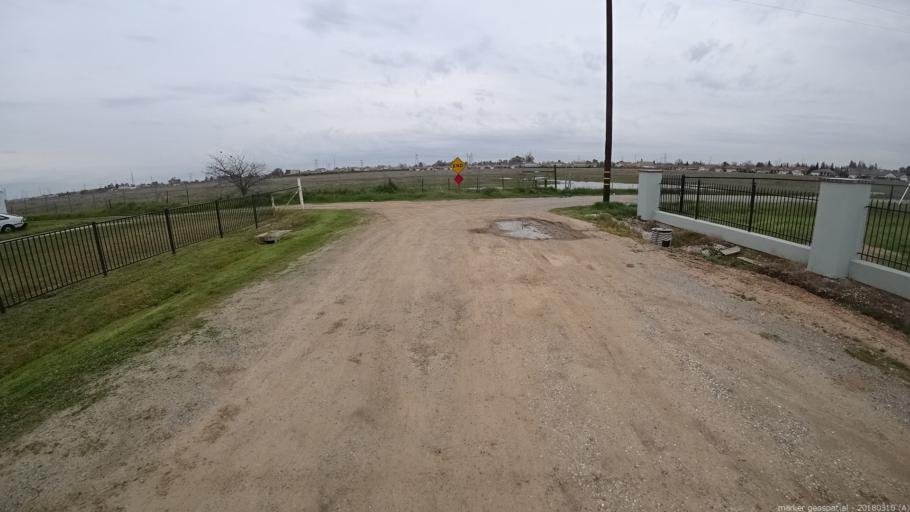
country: US
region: California
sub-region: Sacramento County
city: Vineyard
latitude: 38.4726
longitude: -121.3628
